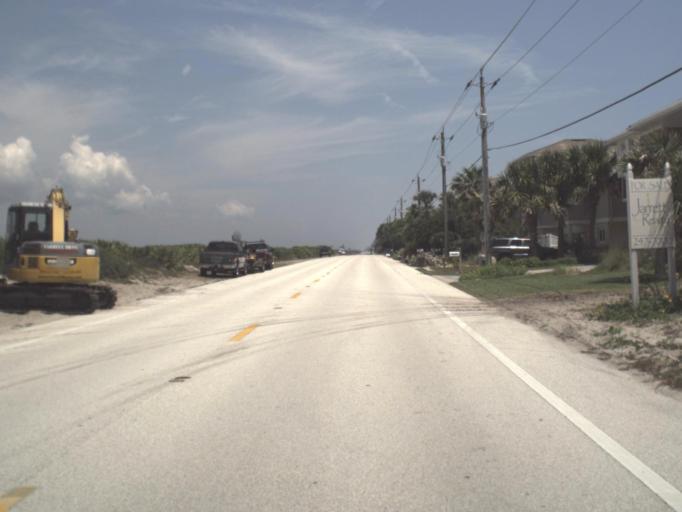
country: US
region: Florida
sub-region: Saint Johns County
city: Villano Beach
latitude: 30.0004
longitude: -81.3177
